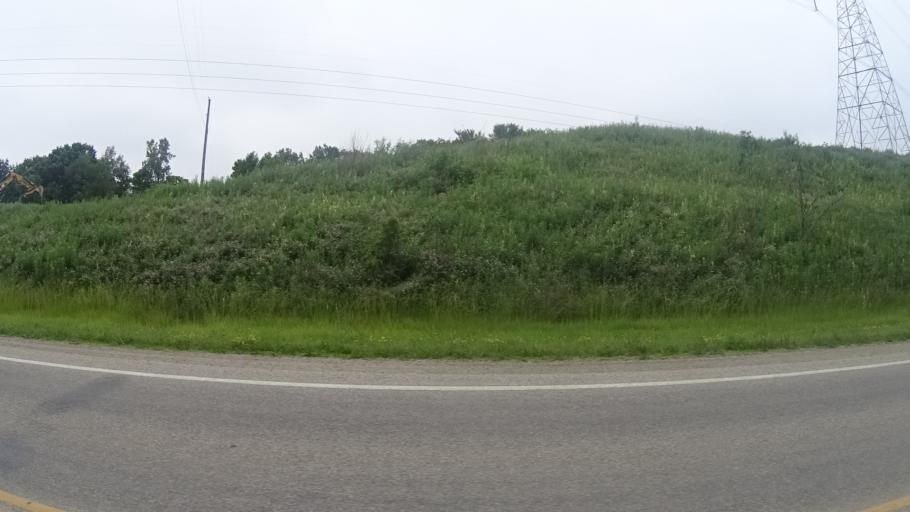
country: US
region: Ohio
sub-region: Erie County
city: Milan
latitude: 41.3365
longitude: -82.5754
